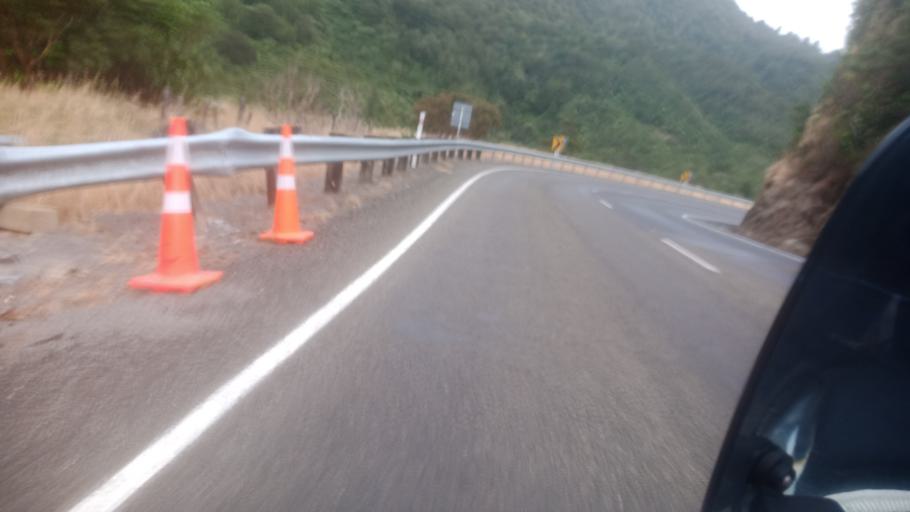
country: NZ
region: Bay of Plenty
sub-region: Opotiki District
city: Opotiki
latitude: -38.3556
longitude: 177.4519
